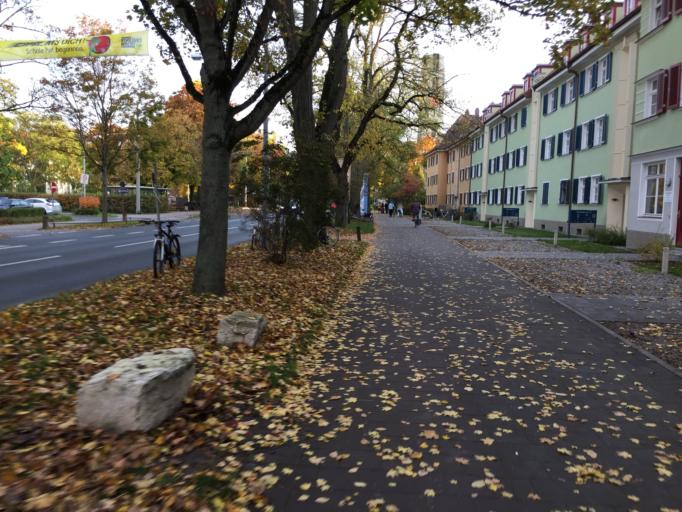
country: DE
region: Bavaria
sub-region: Regierungsbezirk Mittelfranken
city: Erlangen
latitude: 49.5855
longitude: 11.0080
